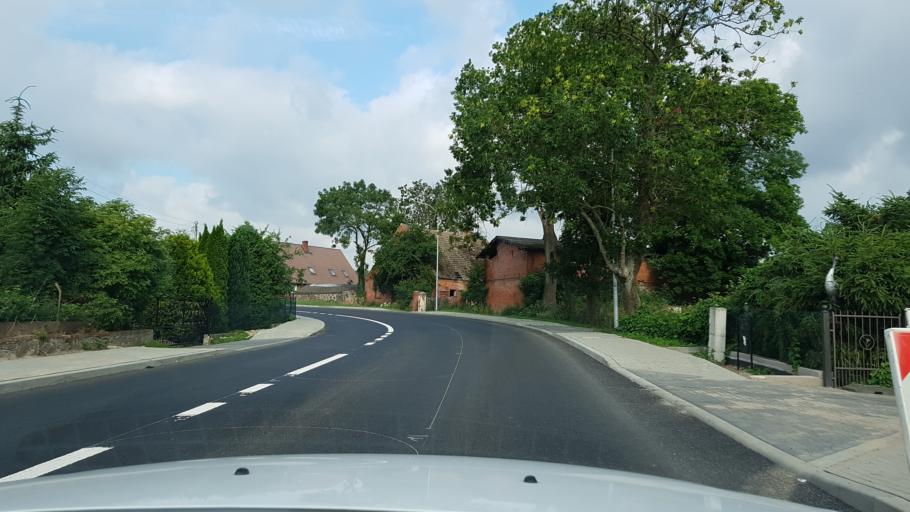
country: PL
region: West Pomeranian Voivodeship
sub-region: Powiat gryfinski
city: Gryfino
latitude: 53.2613
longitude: 14.5795
